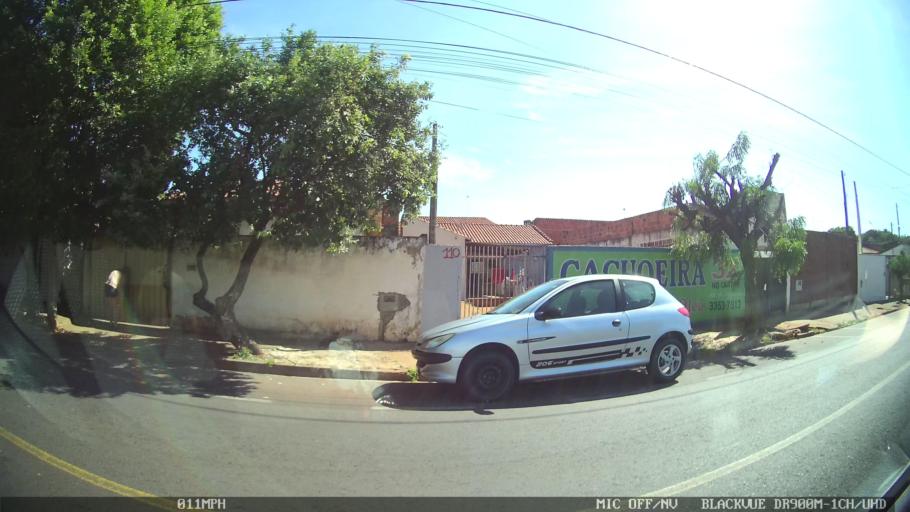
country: BR
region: Sao Paulo
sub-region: Sao Jose Do Rio Preto
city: Sao Jose do Rio Preto
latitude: -20.7711
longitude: -49.4170
